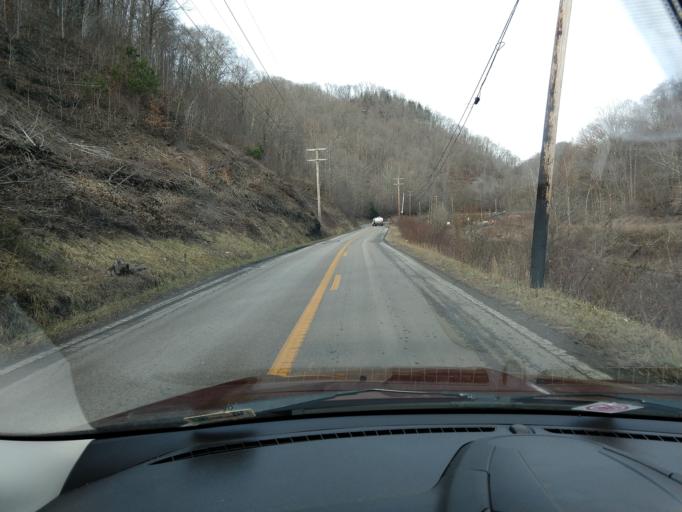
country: US
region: West Virginia
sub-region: McDowell County
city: Welch
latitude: 37.3256
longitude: -81.6881
